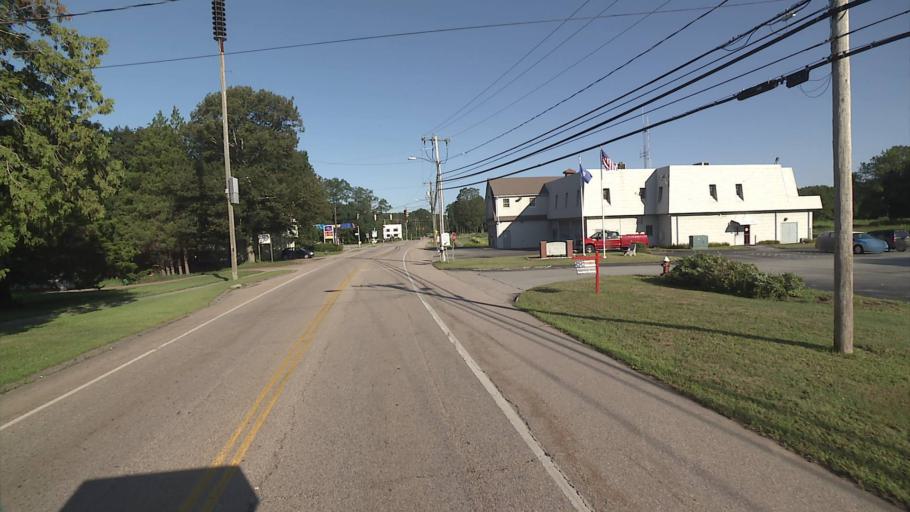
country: US
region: Connecticut
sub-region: New London County
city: Niantic
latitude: 41.3578
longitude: -72.1725
